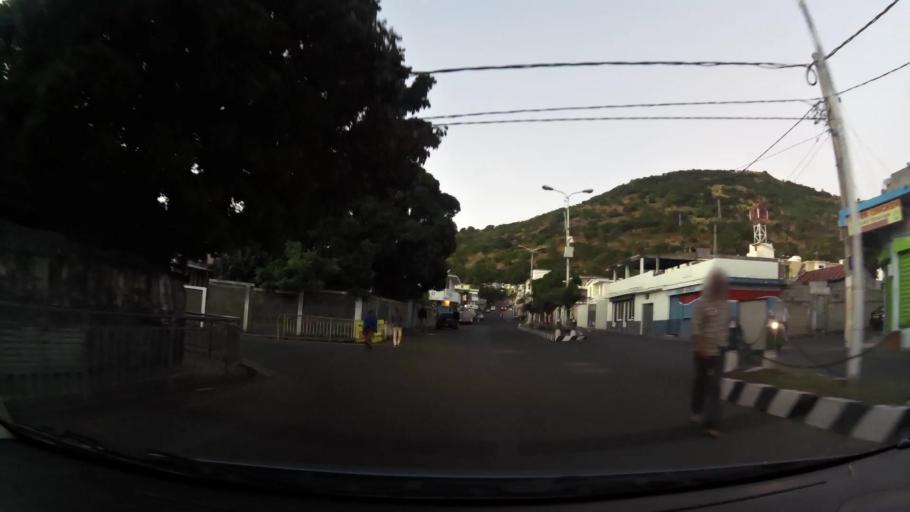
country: MU
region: Port Louis
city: Port Louis
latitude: -20.1654
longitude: 57.5177
